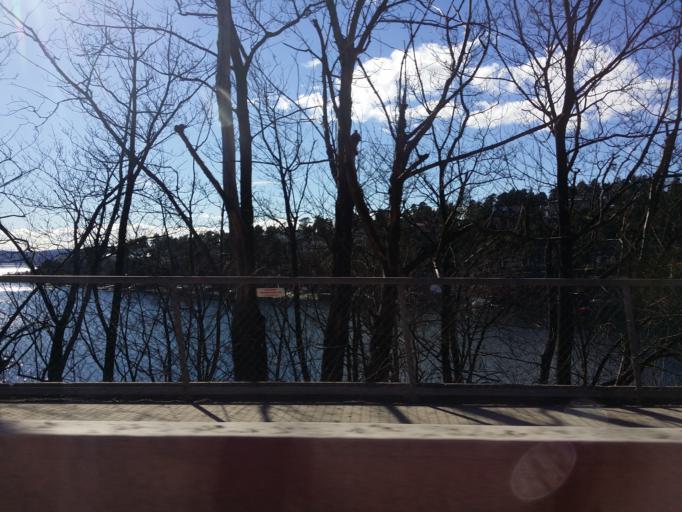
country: NO
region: Oslo
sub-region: Oslo
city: Oslo
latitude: 59.8708
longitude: 10.7808
